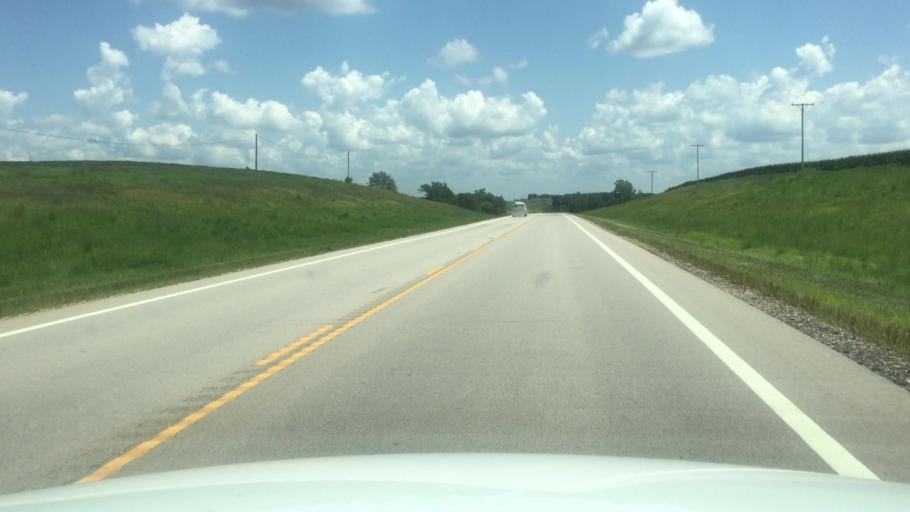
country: US
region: Kansas
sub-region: Brown County
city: Horton
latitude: 39.6673
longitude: -95.4830
